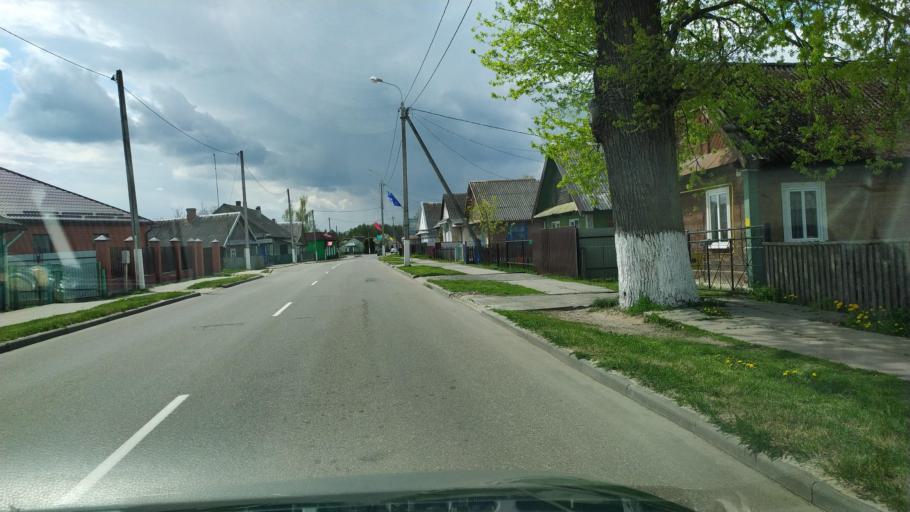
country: BY
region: Brest
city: Pruzhany
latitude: 52.5560
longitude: 24.4491
